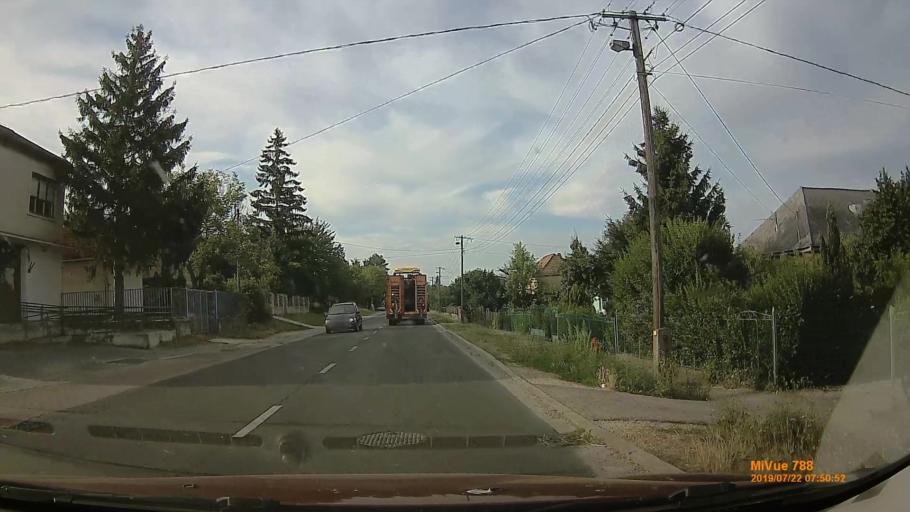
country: HU
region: Veszprem
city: Ajka
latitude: 47.0623
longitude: 17.5531
